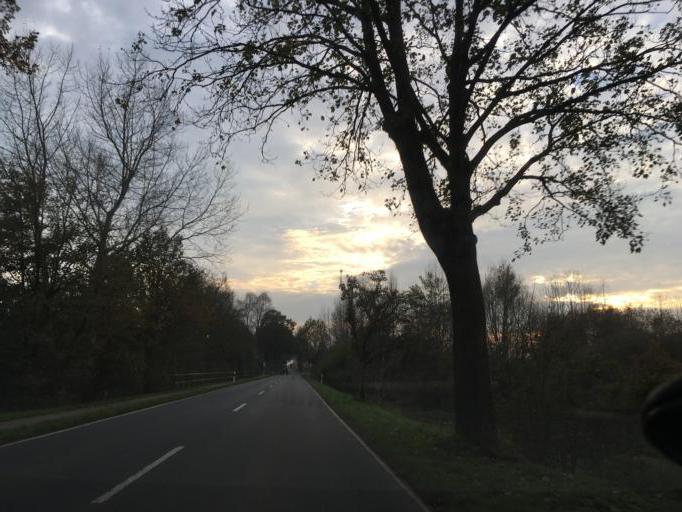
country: DE
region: Lower Saxony
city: Bergen
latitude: 52.8162
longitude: 9.9709
